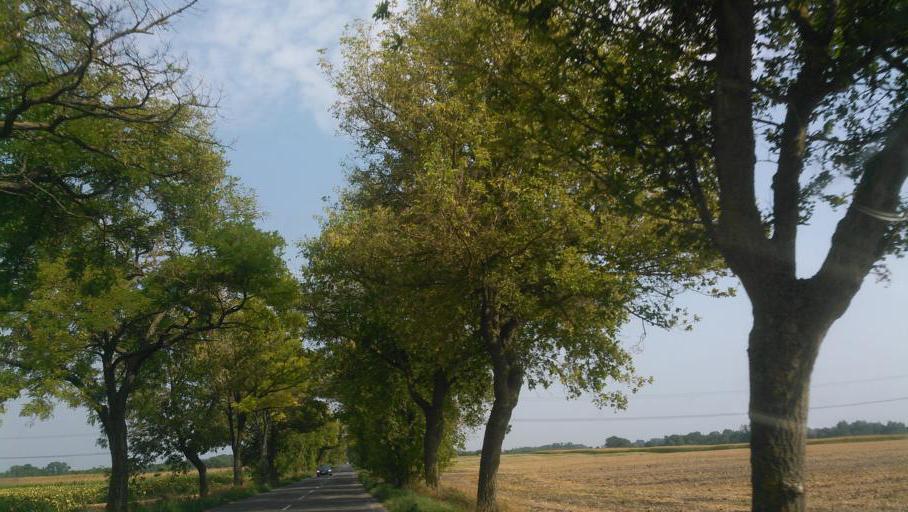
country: SK
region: Trnavsky
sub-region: Okres Dunajska Streda
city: Velky Meder
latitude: 47.9066
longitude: 17.7783
